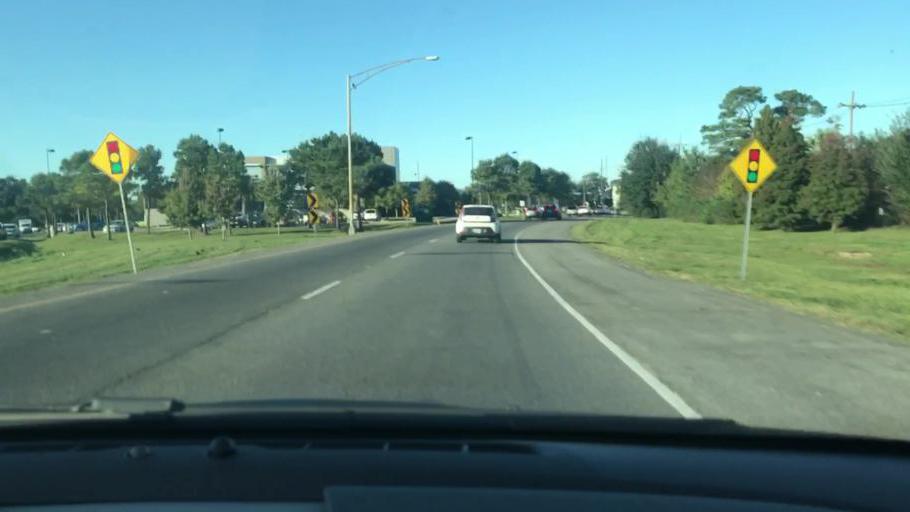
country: US
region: Louisiana
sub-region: Jefferson Parish
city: Metairie
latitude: 29.9977
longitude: -90.1155
